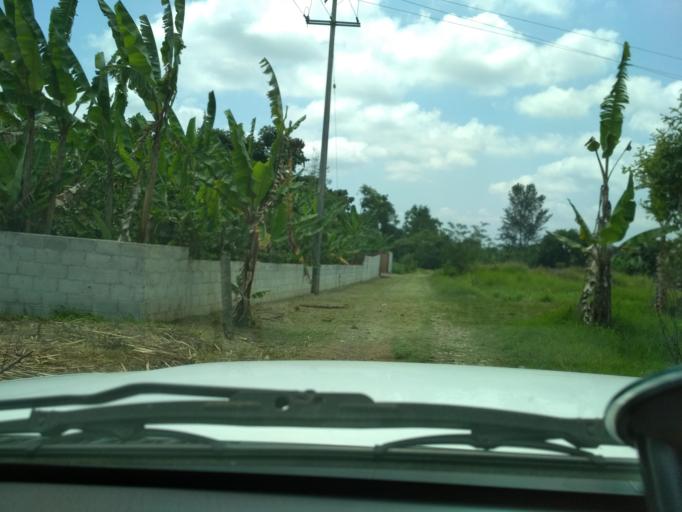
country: MX
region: Veracruz
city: Tocuila
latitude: 18.9559
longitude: -97.0142
